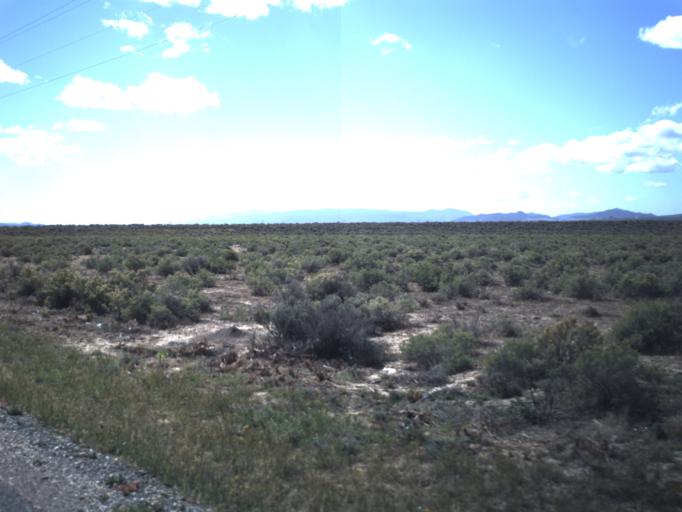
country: US
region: Utah
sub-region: Iron County
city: Enoch
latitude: 37.8274
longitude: -113.0504
